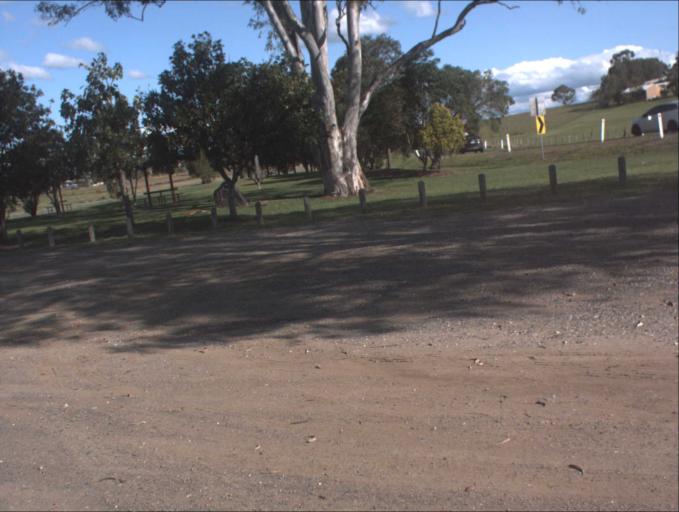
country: AU
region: Queensland
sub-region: Logan
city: Chambers Flat
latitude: -27.7641
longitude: 153.0970
